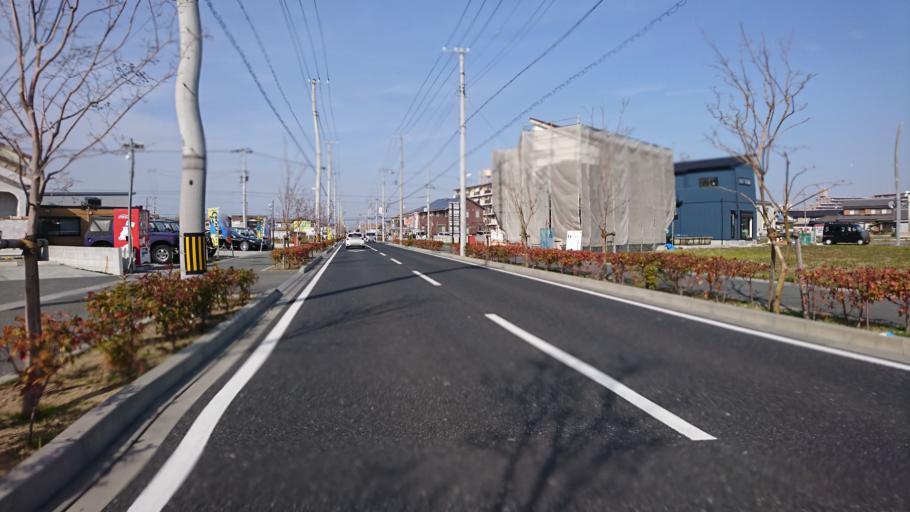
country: JP
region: Hyogo
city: Kakogawacho-honmachi
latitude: 34.7112
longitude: 134.8696
